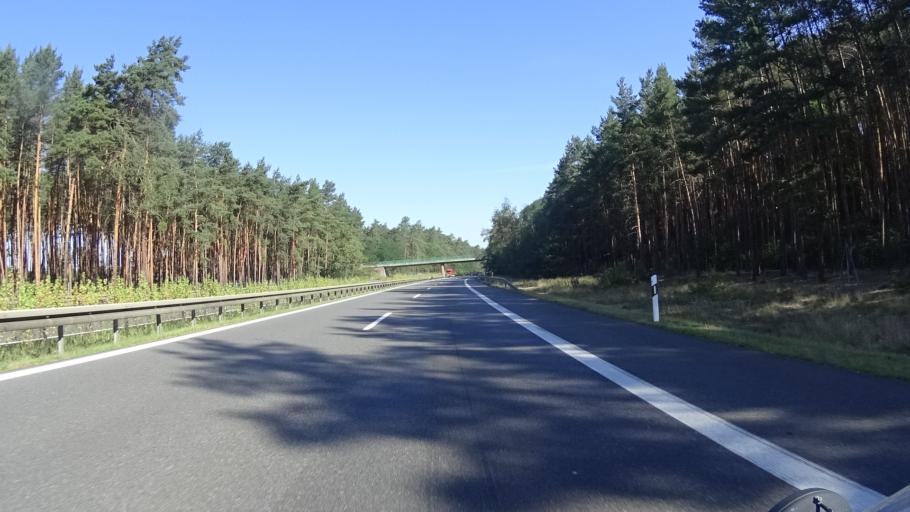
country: DE
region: Brandenburg
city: Bronkow
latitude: 51.7357
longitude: 13.8670
